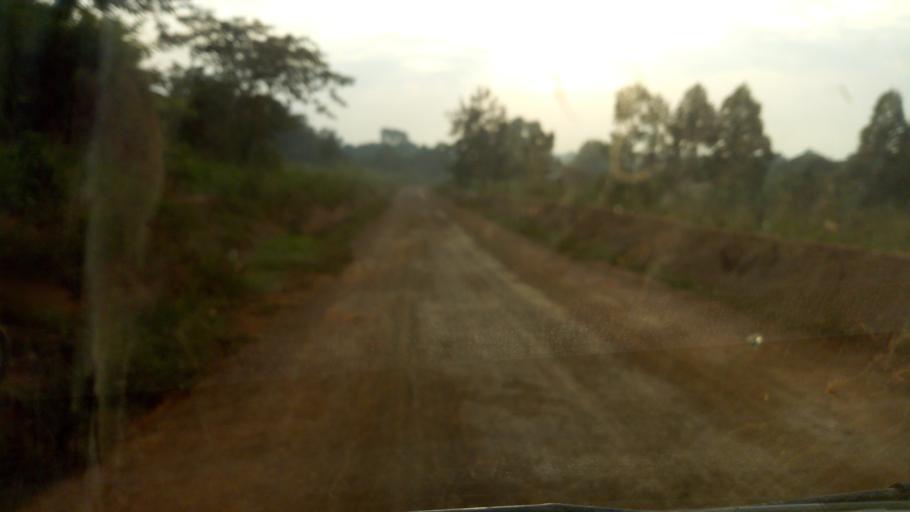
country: UG
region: Western Region
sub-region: Masindi District
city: Masindi
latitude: 1.6744
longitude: 31.7647
